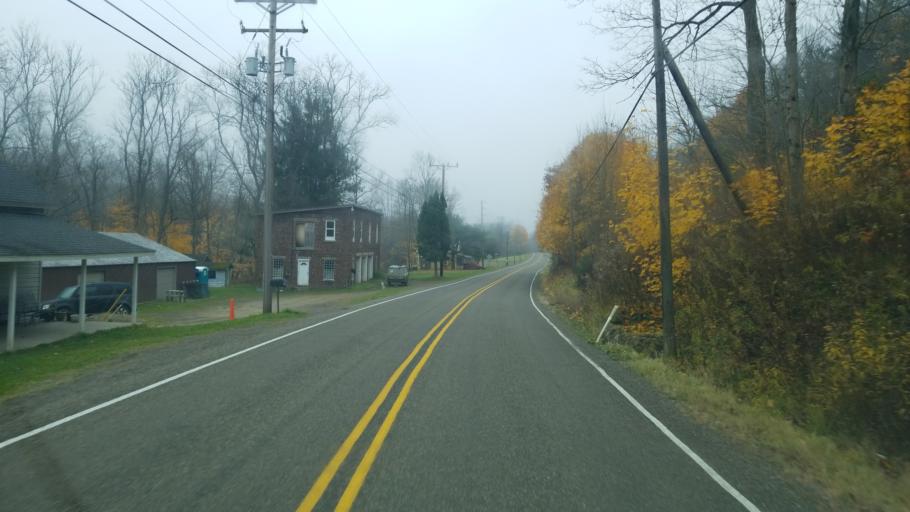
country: US
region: Pennsylvania
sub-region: McKean County
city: Smethport
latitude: 41.8933
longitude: -78.5089
